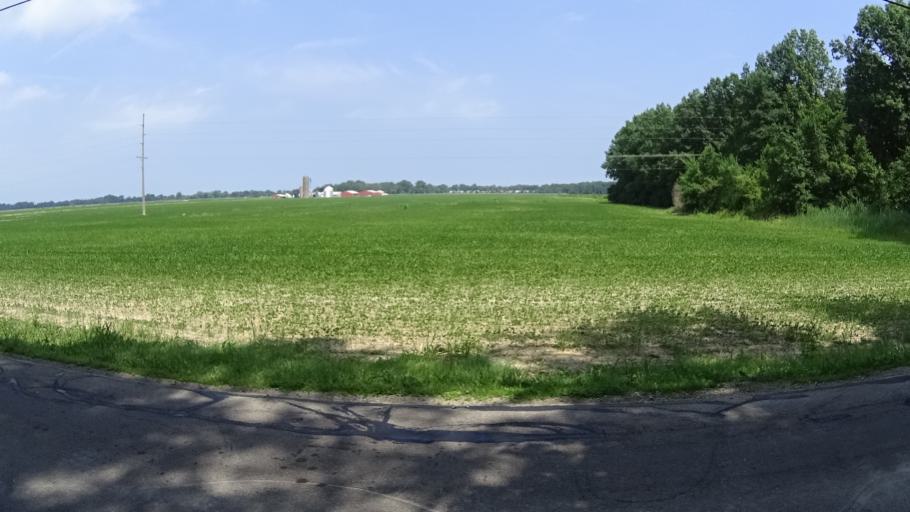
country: US
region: Ohio
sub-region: Lorain County
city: Vermilion
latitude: 41.4011
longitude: -82.3743
